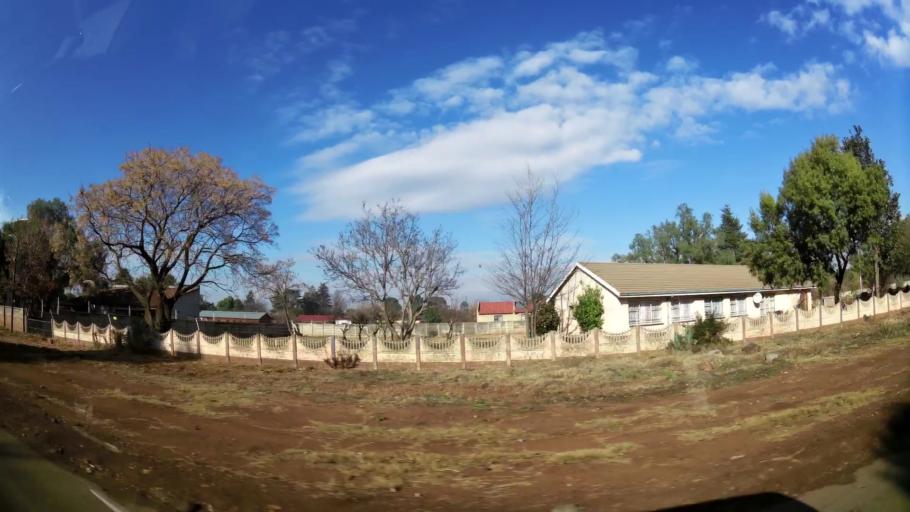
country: ZA
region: Gauteng
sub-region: Sedibeng District Municipality
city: Meyerton
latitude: -26.5025
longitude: 28.0635
